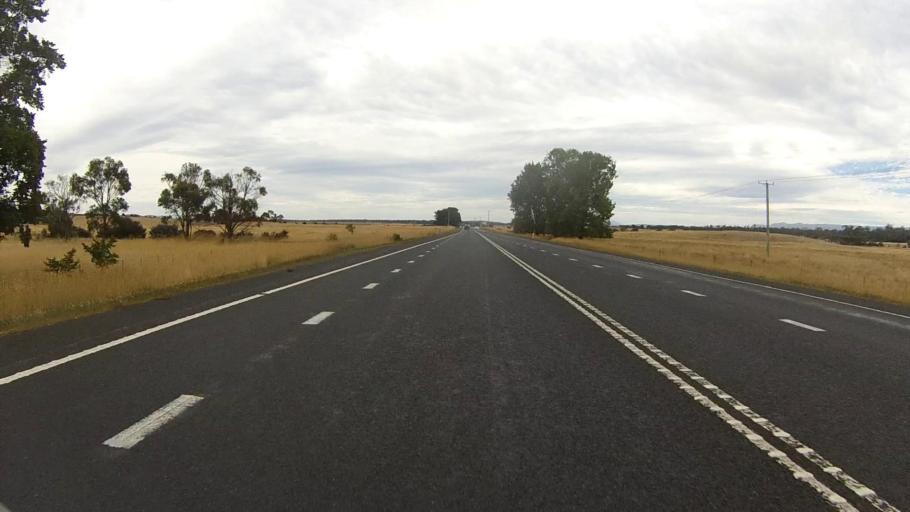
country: AU
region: Tasmania
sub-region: Northern Midlands
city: Evandale
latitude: -41.8679
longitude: 147.4589
